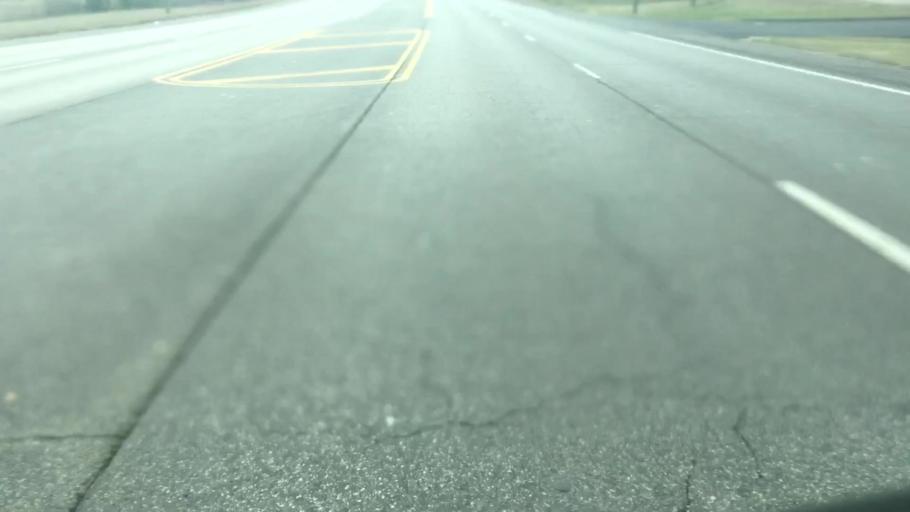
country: US
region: Alabama
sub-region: Walker County
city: Jasper
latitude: 33.8186
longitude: -87.2337
